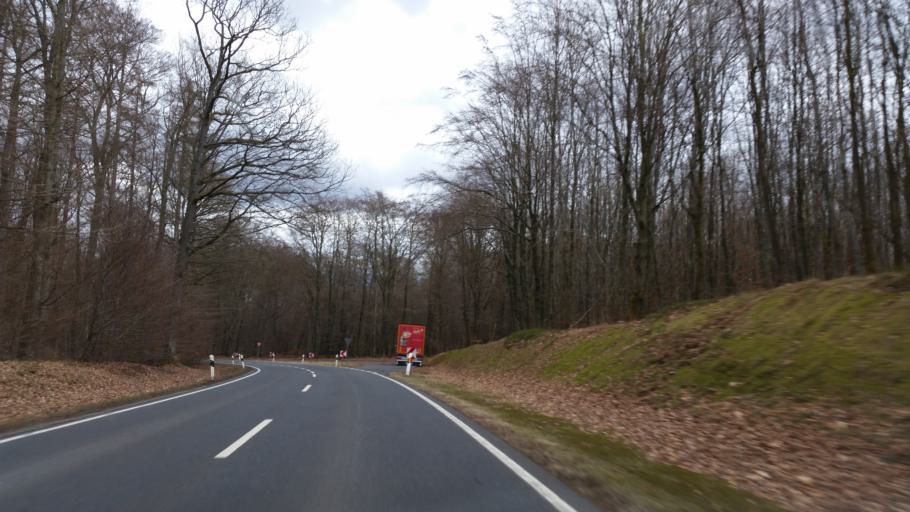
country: DE
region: Bavaria
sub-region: Regierungsbezirk Unterfranken
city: Rothenbuch
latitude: 49.9776
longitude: 9.3657
